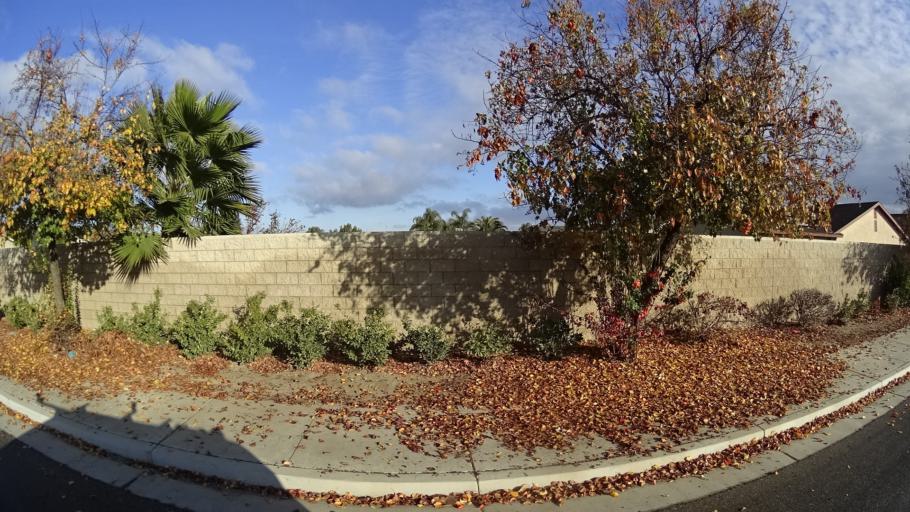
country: US
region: California
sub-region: Kern County
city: Greenfield
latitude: 35.2887
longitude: -118.9961
